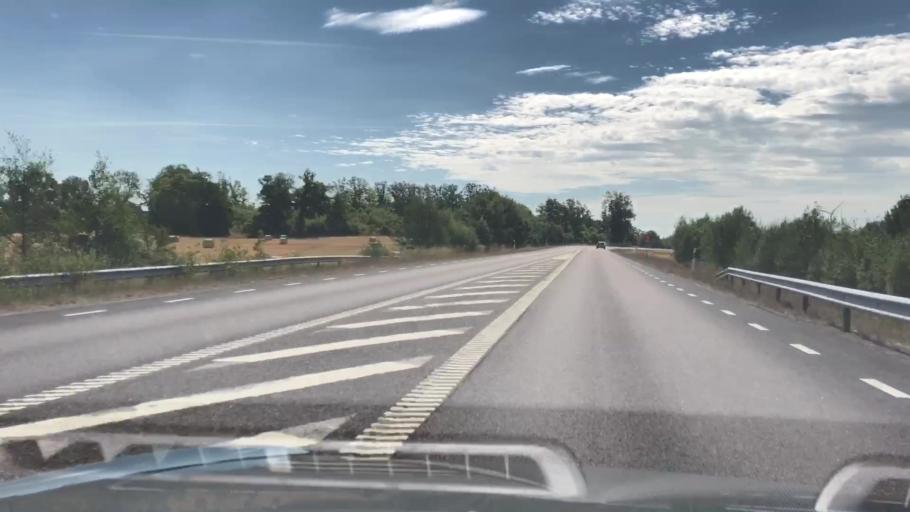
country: SE
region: Kalmar
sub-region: Torsas Kommun
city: Torsas
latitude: 56.4334
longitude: 16.0763
